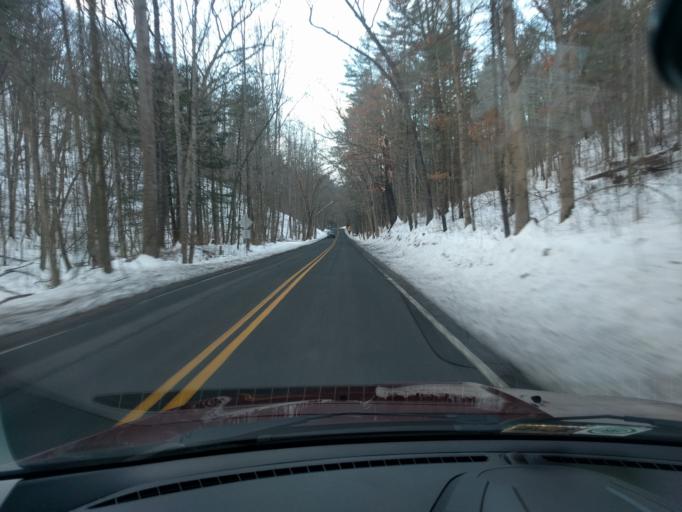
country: US
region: Virginia
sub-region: Bath County
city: Warm Springs
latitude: 38.0820
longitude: -79.8641
